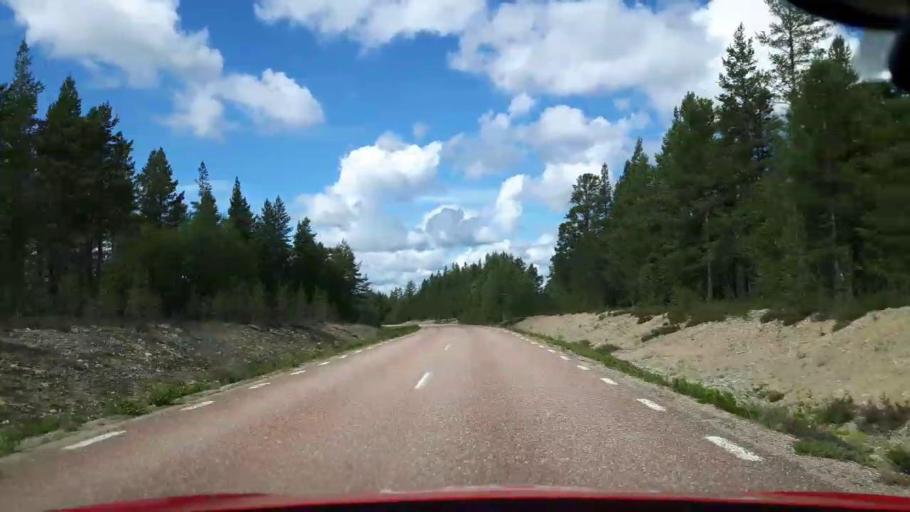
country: SE
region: Dalarna
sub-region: Alvdalens Kommun
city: AElvdalen
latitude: 61.8046
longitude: 13.6543
